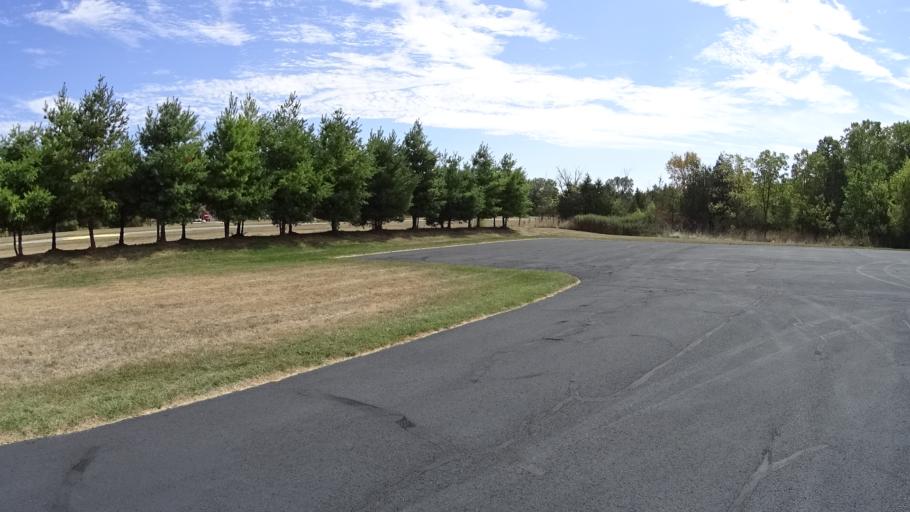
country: US
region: Ohio
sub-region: Erie County
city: Sandusky
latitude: 41.6005
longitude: -82.6882
